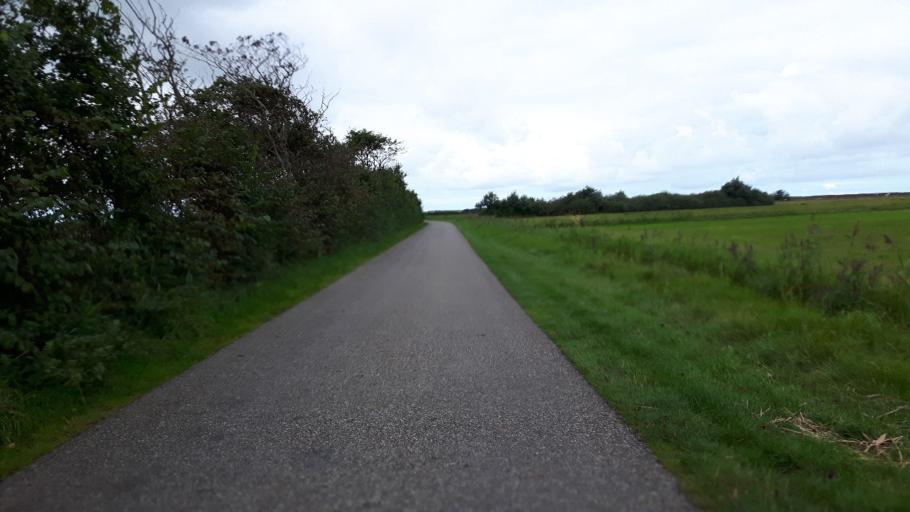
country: NL
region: Friesland
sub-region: Gemeente Ameland
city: Hollum
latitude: 53.4425
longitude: 5.6836
